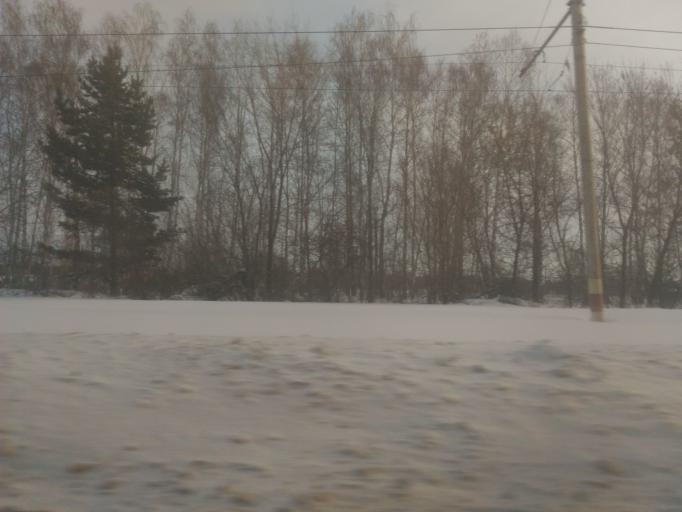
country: RU
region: Ulyanovsk
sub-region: Ulyanovskiy Rayon
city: Ulyanovsk
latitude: 54.3664
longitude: 48.3228
